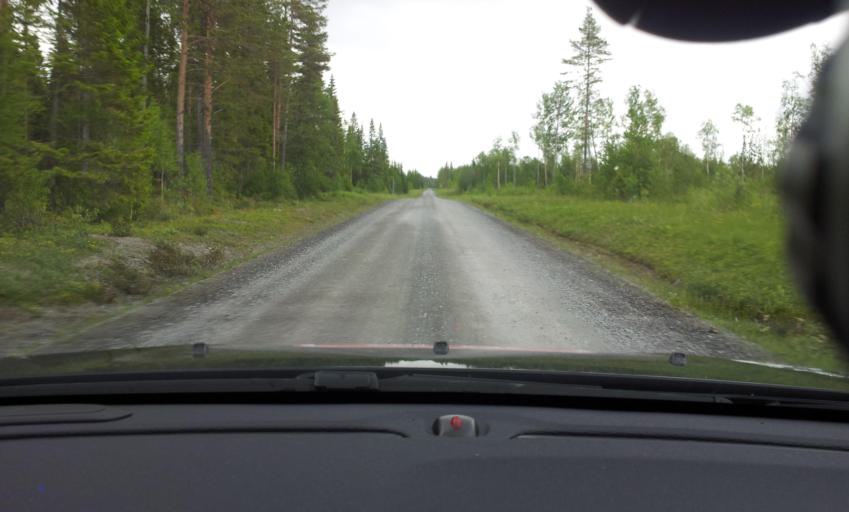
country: SE
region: Jaemtland
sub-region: OEstersunds Kommun
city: Brunflo
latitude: 63.1451
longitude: 15.0452
